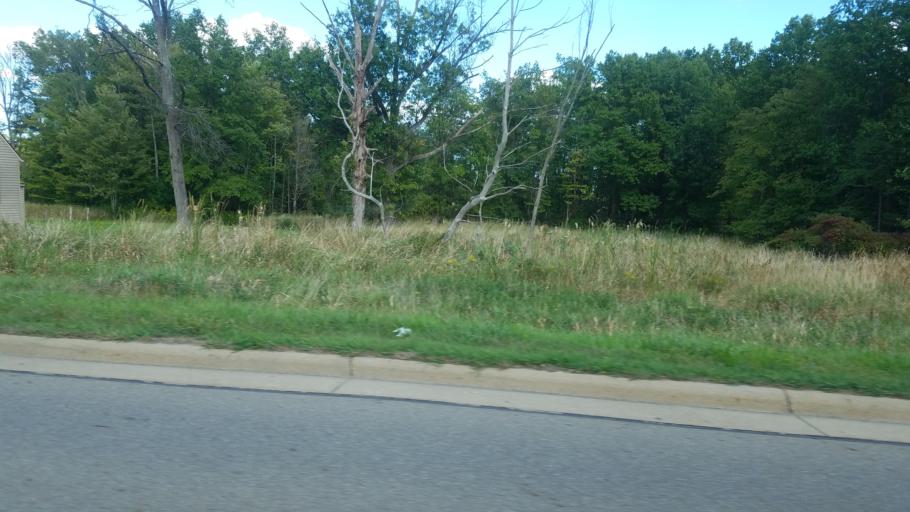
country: US
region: Ohio
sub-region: Mahoning County
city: Austintown
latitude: 41.1129
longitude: -80.7676
